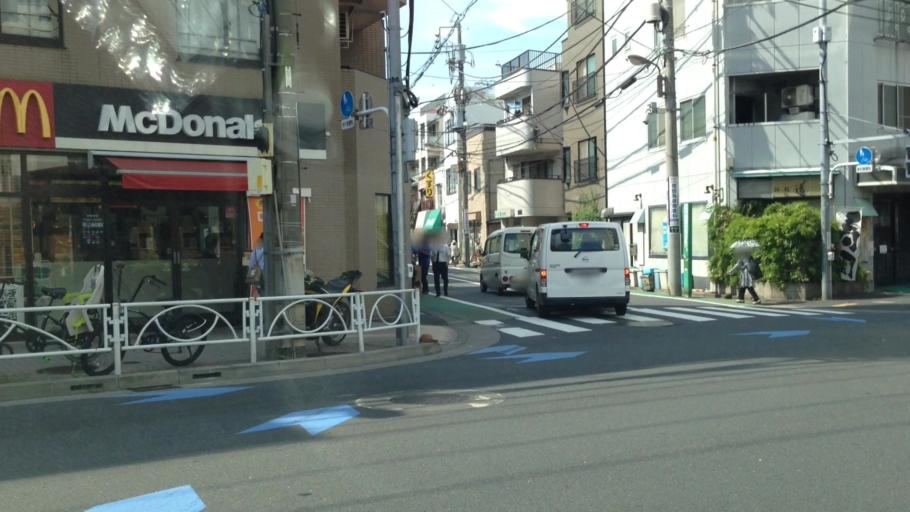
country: JP
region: Tokyo
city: Urayasu
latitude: 35.7181
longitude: 139.8181
